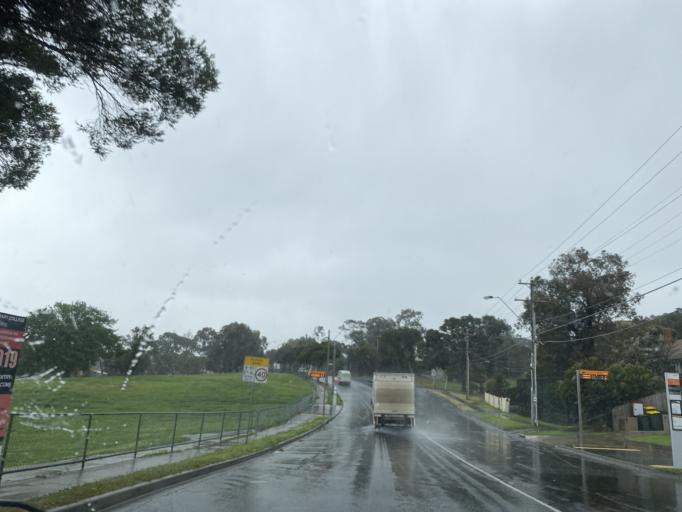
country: AU
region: Victoria
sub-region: Banyule
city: Montmorency
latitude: -37.7139
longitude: 145.1150
